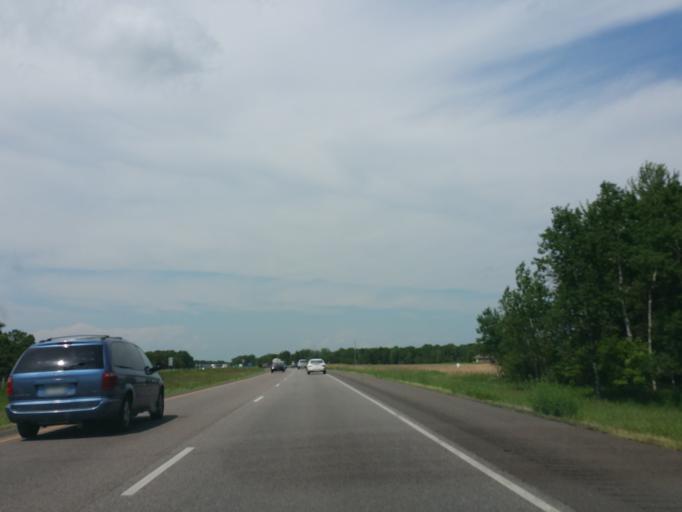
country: US
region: Minnesota
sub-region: Chisago County
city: Stacy
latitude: 45.4374
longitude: -92.9893
